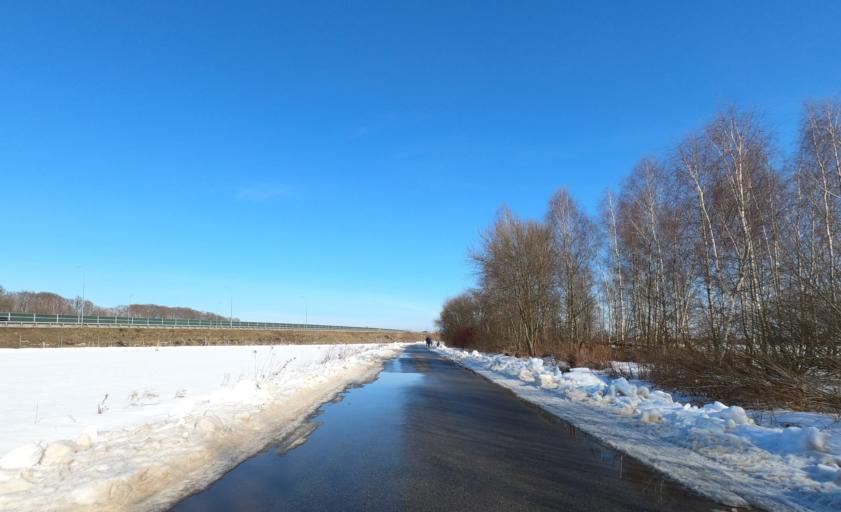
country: PL
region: Subcarpathian Voivodeship
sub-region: Powiat debicki
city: Brzeznica
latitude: 50.0790
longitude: 21.4787
